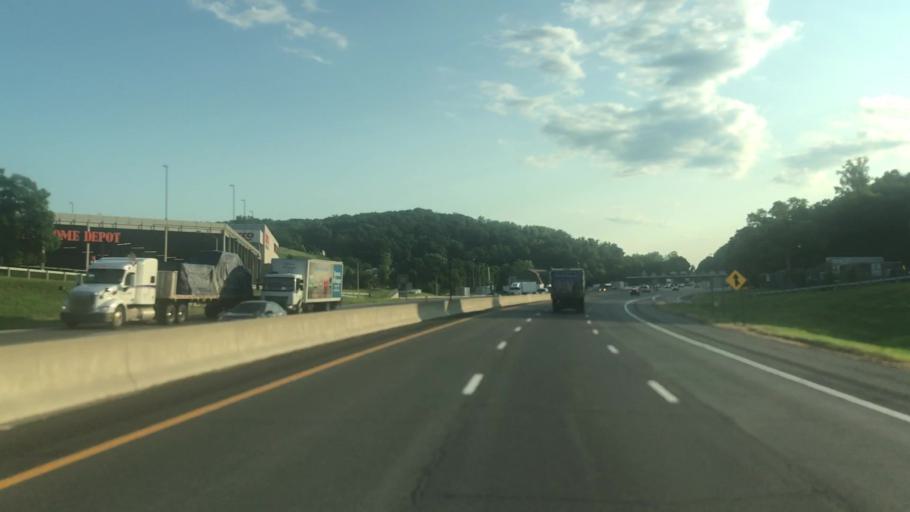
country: US
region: New York
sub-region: Westchester County
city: Hastings-on-Hudson
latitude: 40.9720
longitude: -73.8610
